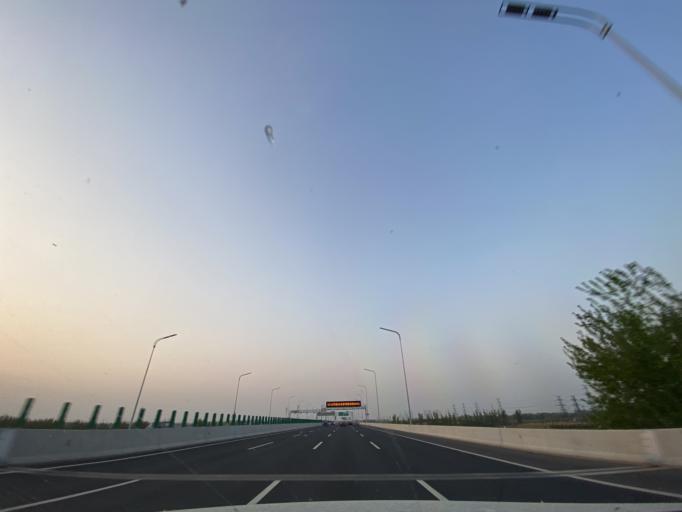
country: CN
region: Beijing
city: Xingfeng
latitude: 39.7038
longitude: 116.3789
